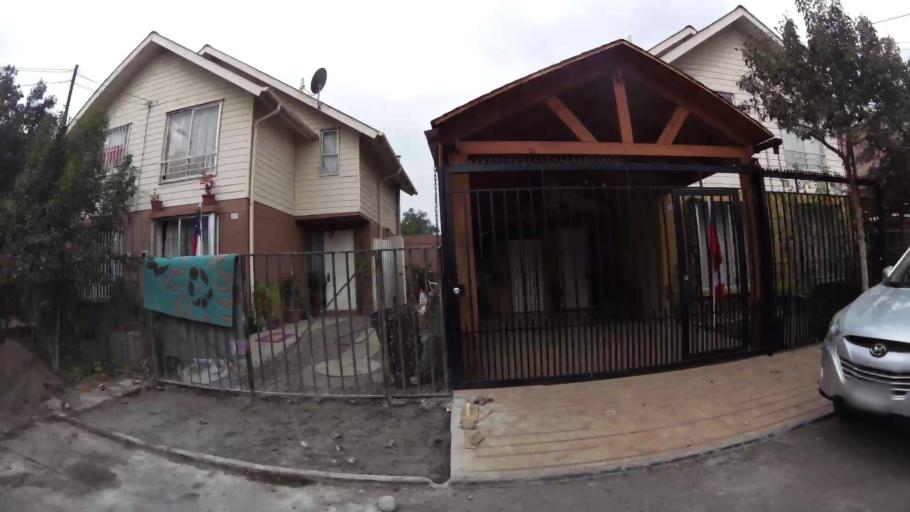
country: CL
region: Santiago Metropolitan
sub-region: Provincia de Chacabuco
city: Chicureo Abajo
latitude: -33.2014
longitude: -70.6805
